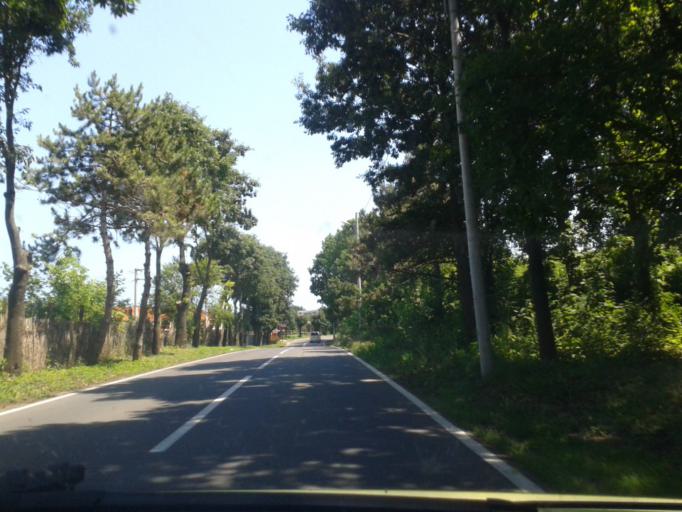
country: RO
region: Constanta
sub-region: Comuna Douazeci si Trei August
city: Douazeci si Trei August
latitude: 43.8948
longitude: 28.5966
